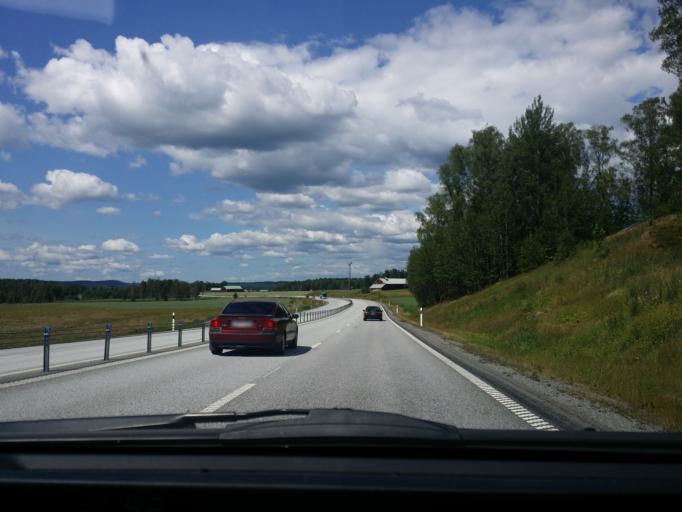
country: SE
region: OErebro
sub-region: Orebro Kommun
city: Hovsta
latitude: 59.3956
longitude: 15.2045
